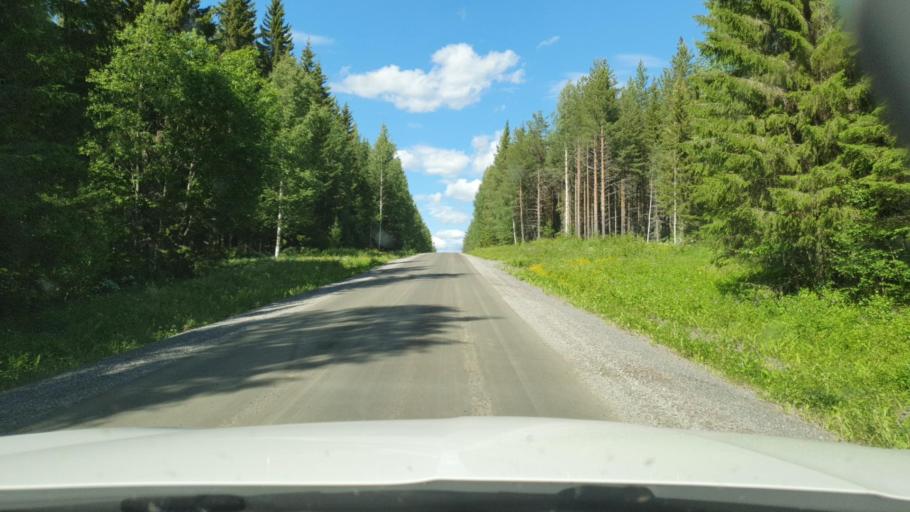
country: SE
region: Vaesterbotten
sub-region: Skelleftea Kommun
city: Forsbacka
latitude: 64.7965
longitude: 20.5058
